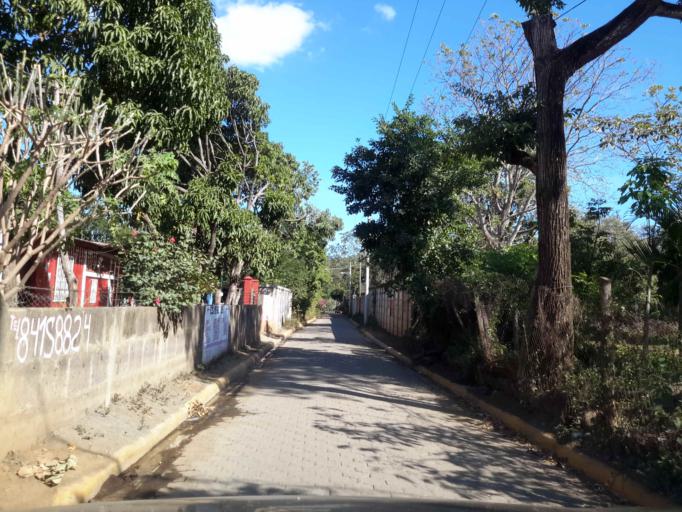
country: NI
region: Managua
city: Managua
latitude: 12.0832
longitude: -86.2358
